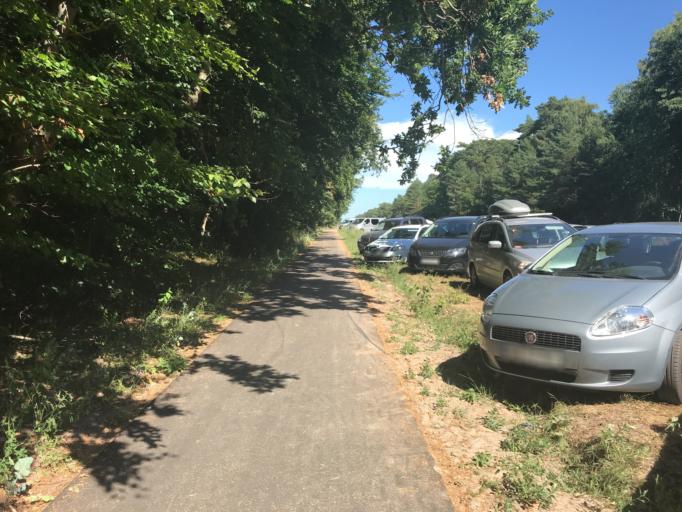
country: PL
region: West Pomeranian Voivodeship
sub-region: Powiat slawienski
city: Darlowo
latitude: 54.5193
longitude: 16.4905
